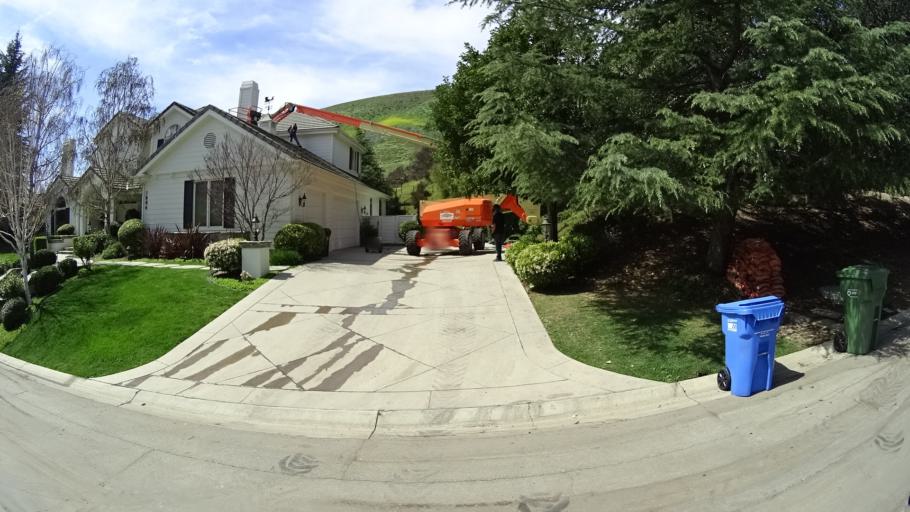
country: US
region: California
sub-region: Ventura County
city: Thousand Oaks
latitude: 34.1836
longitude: -118.8244
